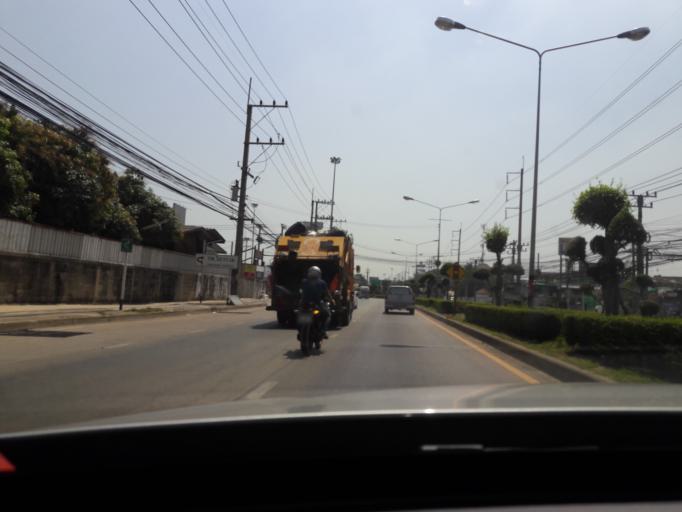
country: TH
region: Samut Sakhon
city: Samut Sakhon
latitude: 13.5639
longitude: 100.2721
